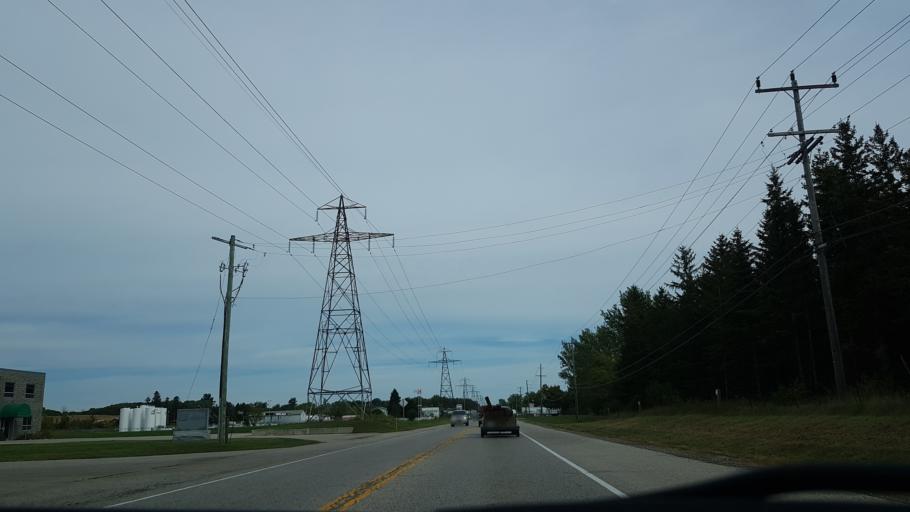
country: CA
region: Ontario
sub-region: Wellington County
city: Guelph
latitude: 43.4925
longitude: -80.2820
